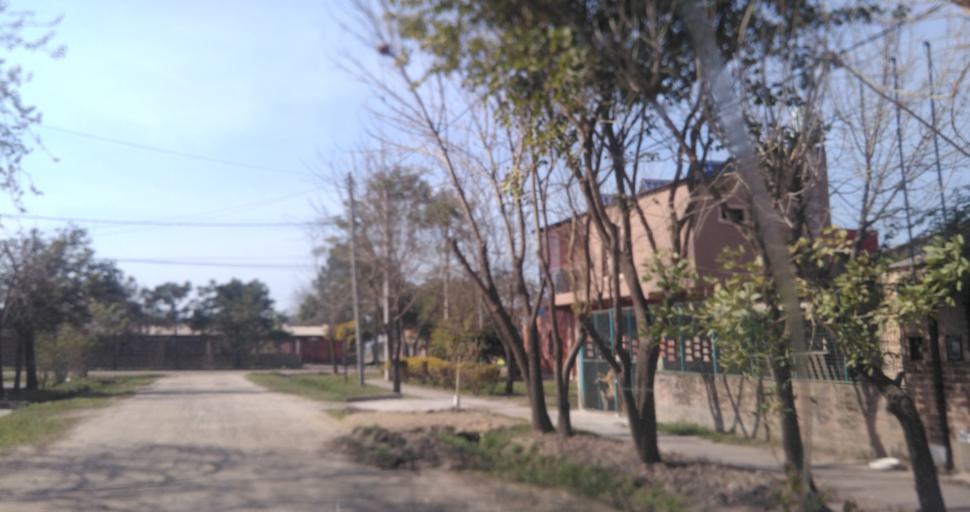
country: AR
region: Chaco
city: Fontana
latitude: -27.4464
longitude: -59.0357
